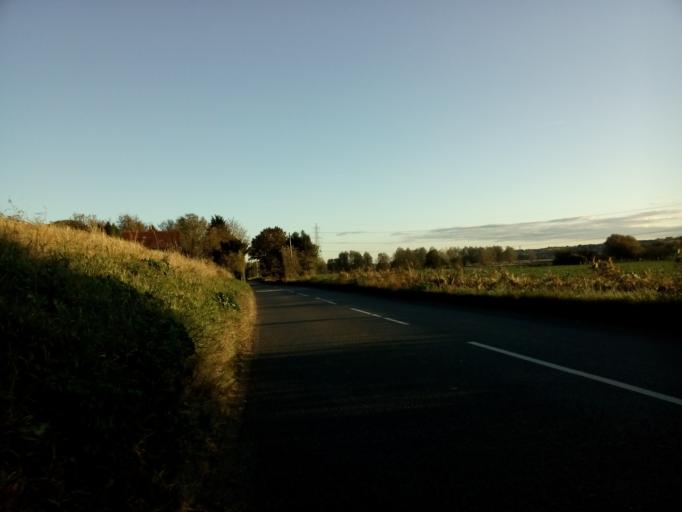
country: GB
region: England
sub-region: Suffolk
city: Sudbury
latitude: 52.0041
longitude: 0.7550
